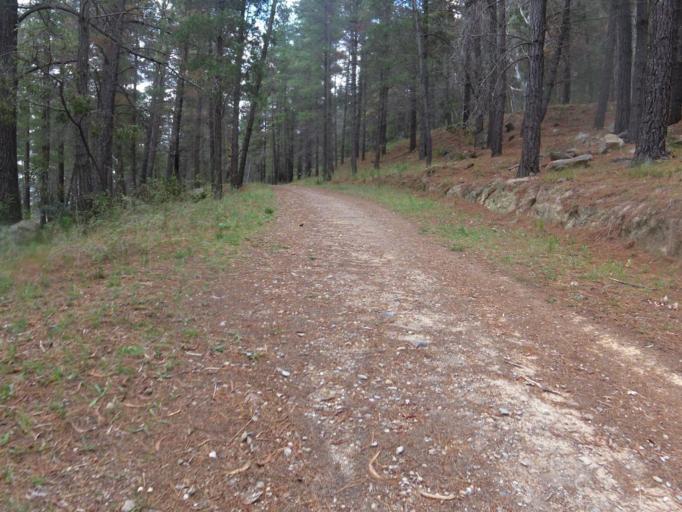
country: AU
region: Australian Capital Territory
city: Macarthur
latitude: -35.3665
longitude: 149.1149
